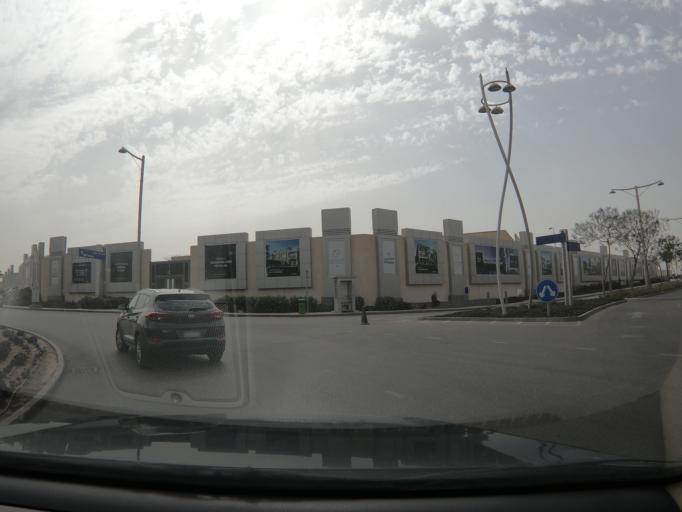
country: EG
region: Muhafazat al Qahirah
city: Cairo
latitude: 30.0305
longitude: 31.4060
